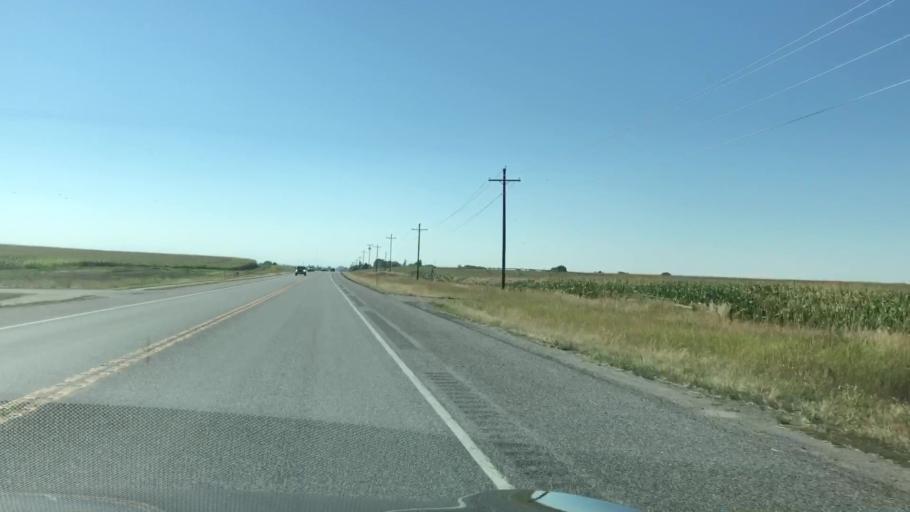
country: US
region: Montana
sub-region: Gallatin County
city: Bozeman
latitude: 45.7291
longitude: -111.1037
